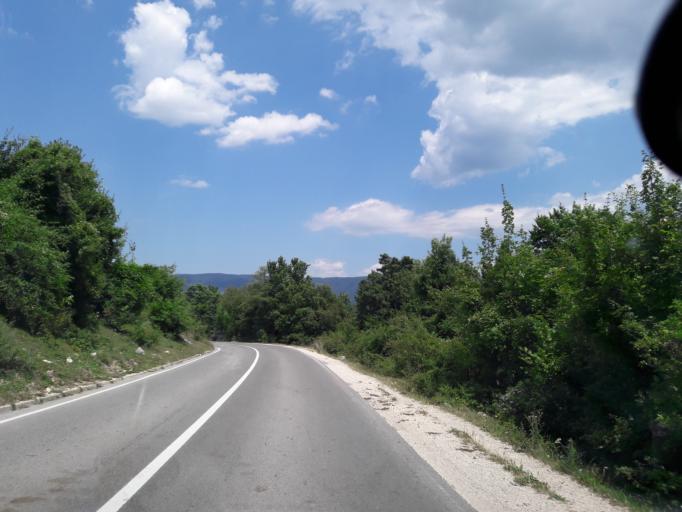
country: BA
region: Republika Srpska
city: Sipovo
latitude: 44.1824
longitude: 17.1606
